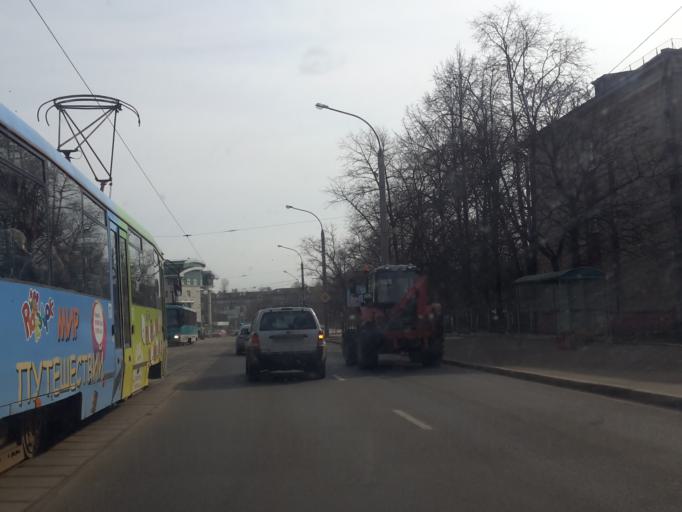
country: BY
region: Minsk
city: Minsk
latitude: 53.9040
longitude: 27.5978
